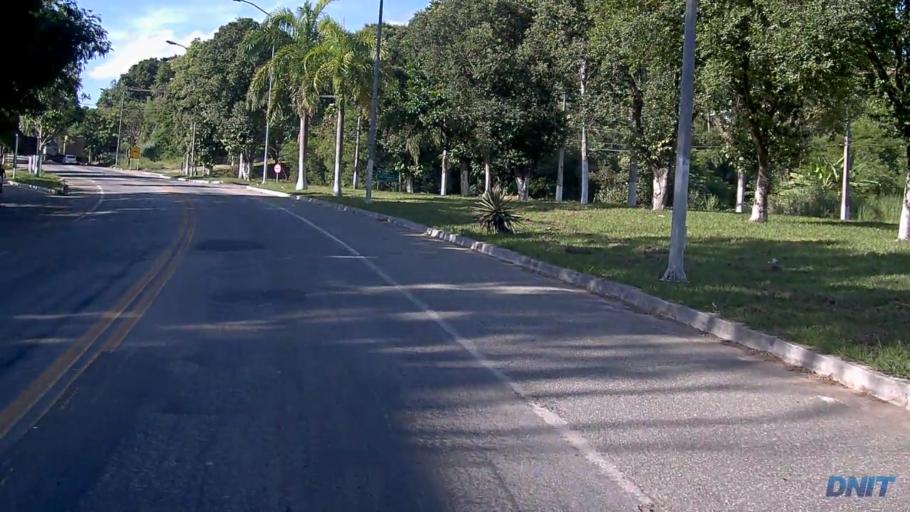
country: BR
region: Minas Gerais
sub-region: Belo Oriente
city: Belo Oriente
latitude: -19.2294
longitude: -42.3264
